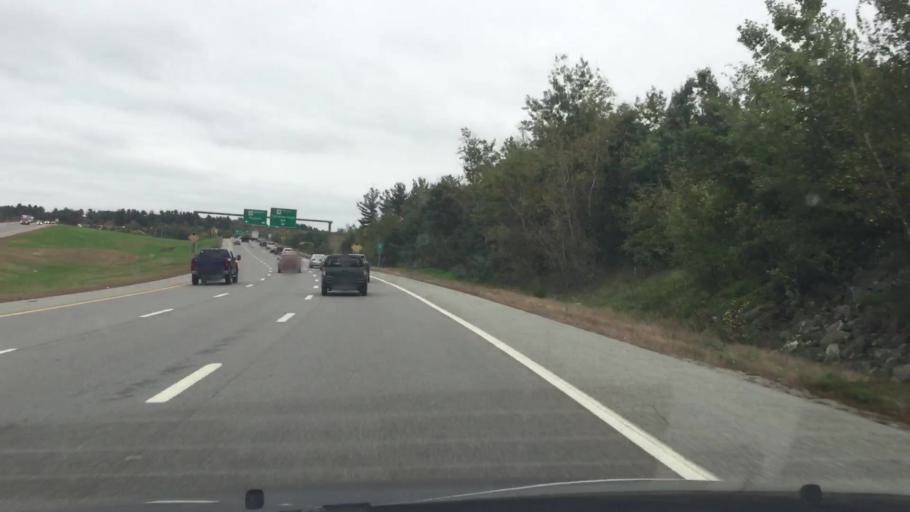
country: US
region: New Hampshire
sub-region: Hillsborough County
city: Hudson
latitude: 42.7248
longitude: -71.4334
